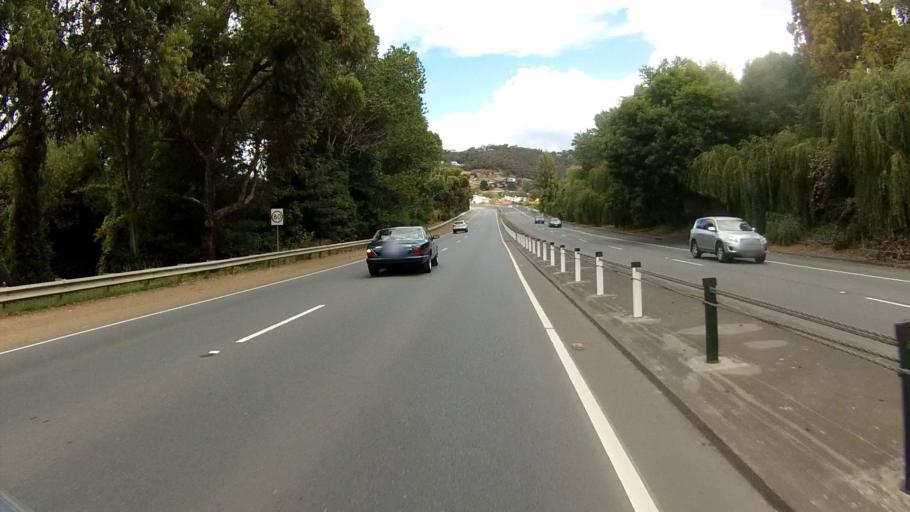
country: AU
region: Tasmania
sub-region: Hobart
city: Sandy Bay
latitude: -42.8968
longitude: 147.3171
